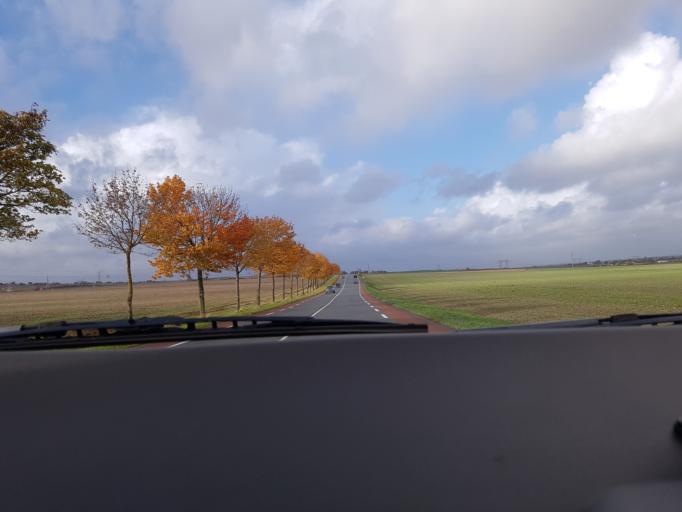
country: FR
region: Poitou-Charentes
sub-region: Departement de la Charente-Maritime
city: Les Gonds
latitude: 45.6609
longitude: -0.5931
